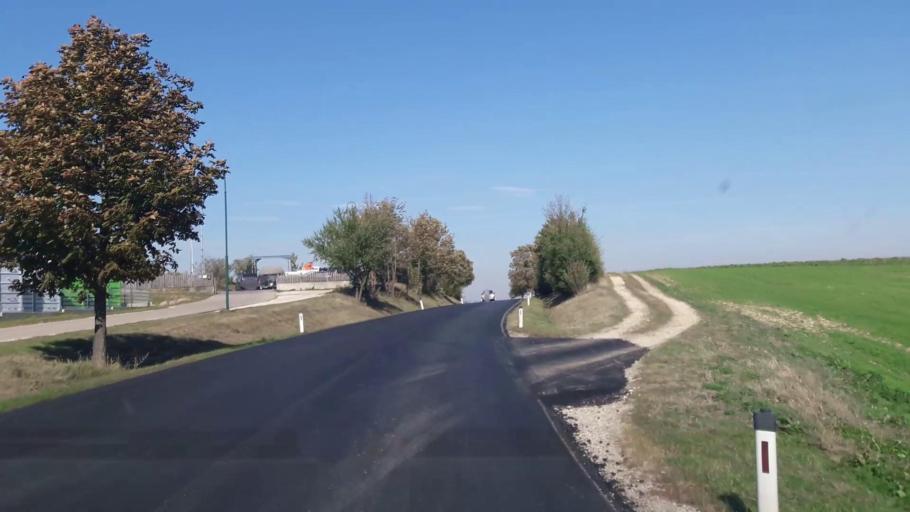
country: AT
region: Lower Austria
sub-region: Politischer Bezirk Korneuburg
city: Grossrussbach
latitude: 48.4651
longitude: 16.3780
